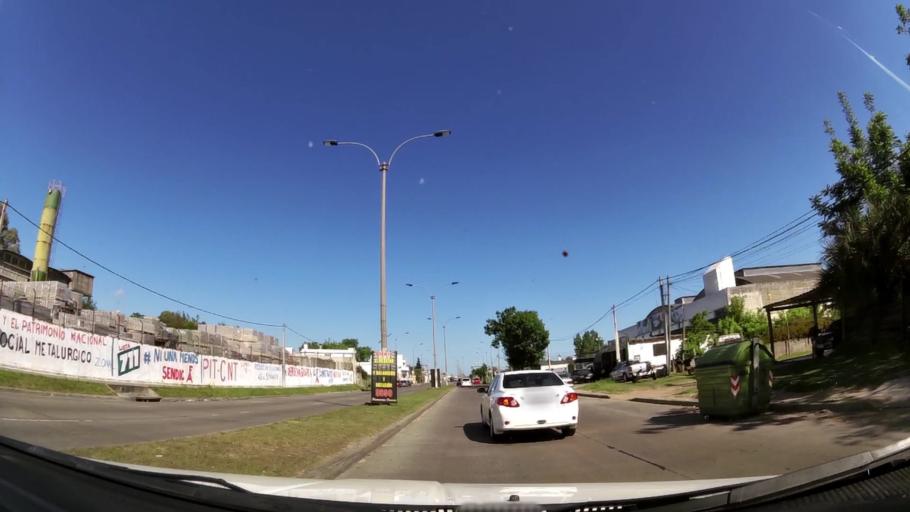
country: UY
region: Montevideo
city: Montevideo
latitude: -34.8352
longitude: -56.2070
